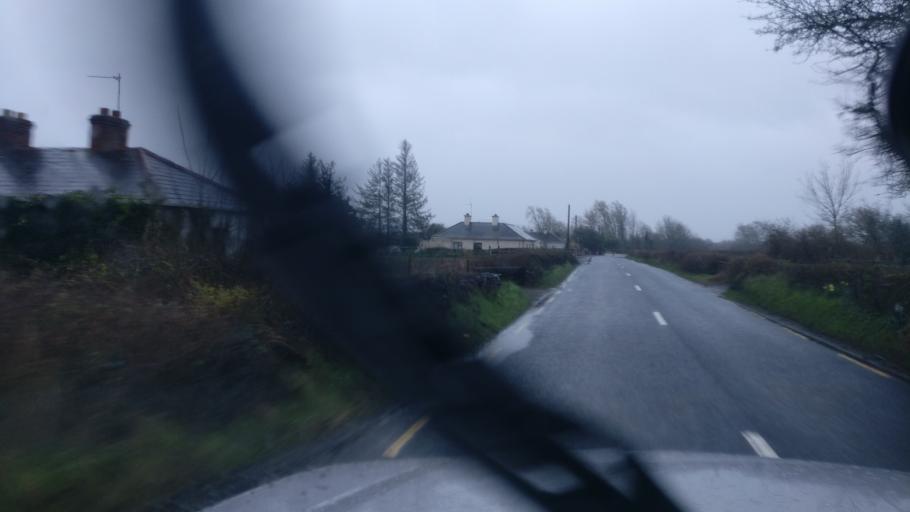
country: IE
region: Connaught
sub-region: County Galway
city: Ballinasloe
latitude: 53.2775
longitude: -8.2113
